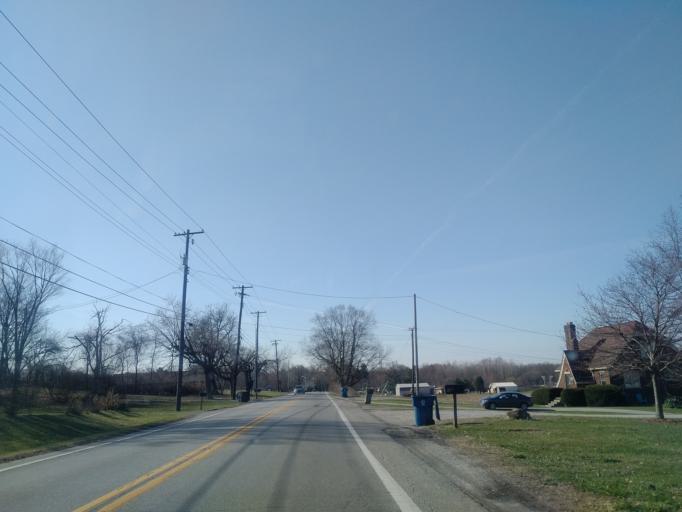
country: US
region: Indiana
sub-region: Marion County
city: Southport
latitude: 39.6829
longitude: -86.1751
